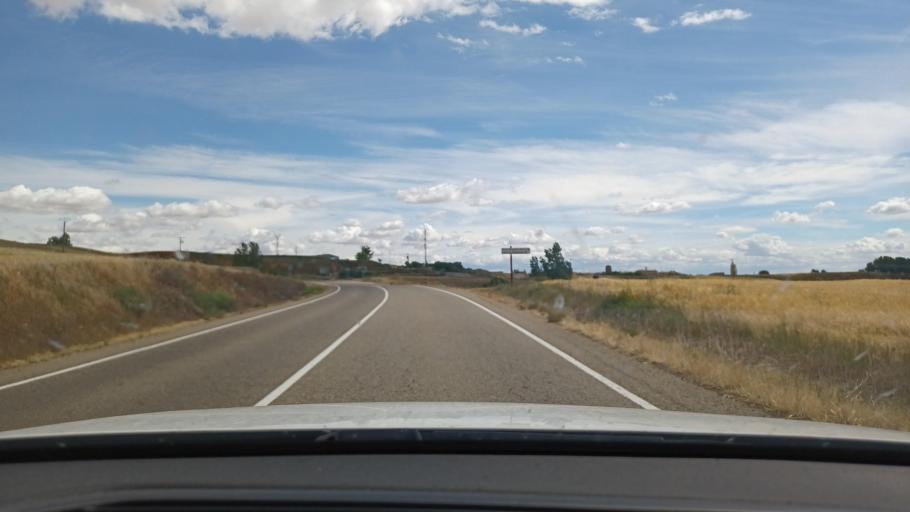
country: ES
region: Castille and Leon
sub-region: Provincia de Leon
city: Sahagun
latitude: 42.3812
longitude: -5.0274
